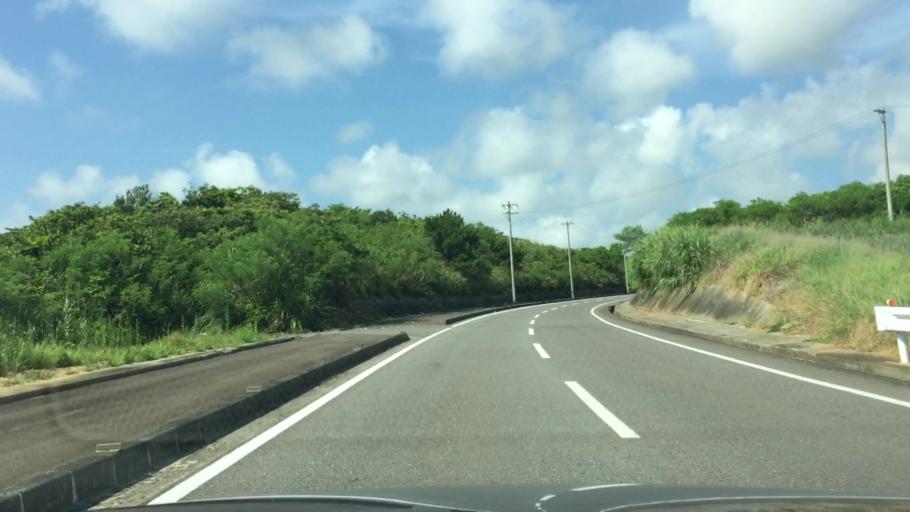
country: JP
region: Okinawa
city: Ishigaki
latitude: 24.4120
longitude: 124.2297
